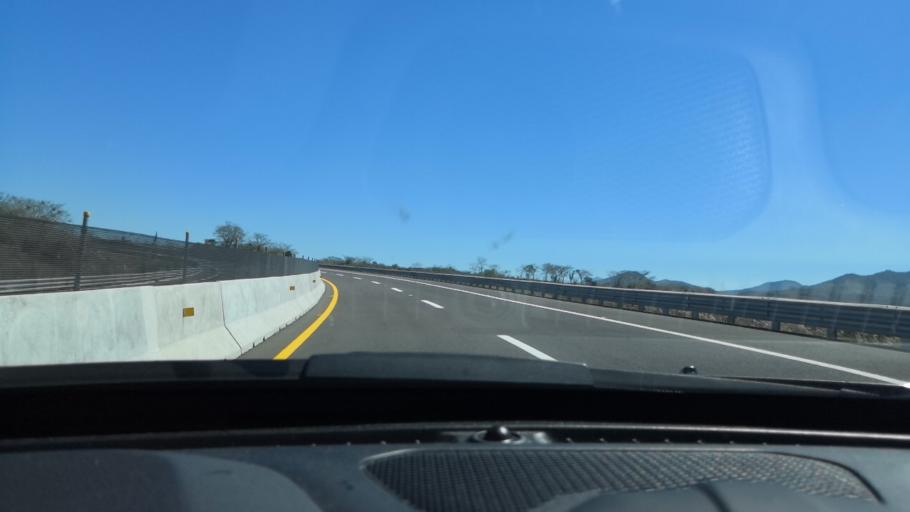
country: MX
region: Nayarit
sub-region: Compostela
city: Juan Escutia (Borbollon)
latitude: 21.1178
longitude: -104.8871
